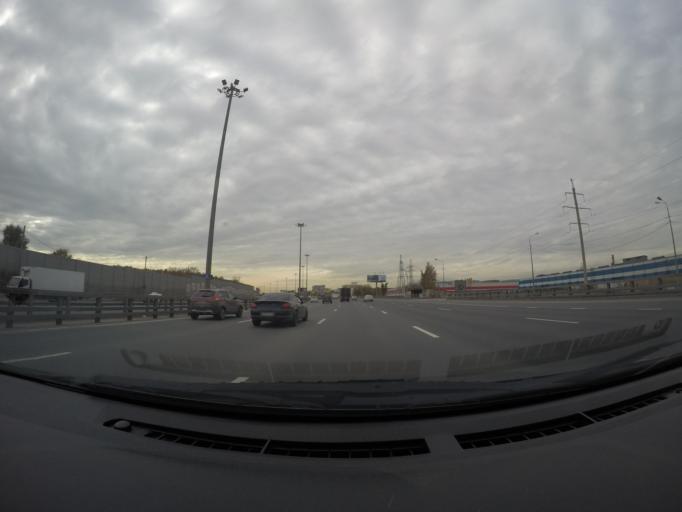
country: RU
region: Moskovskaya
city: Druzhba
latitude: 55.9068
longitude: 37.7649
